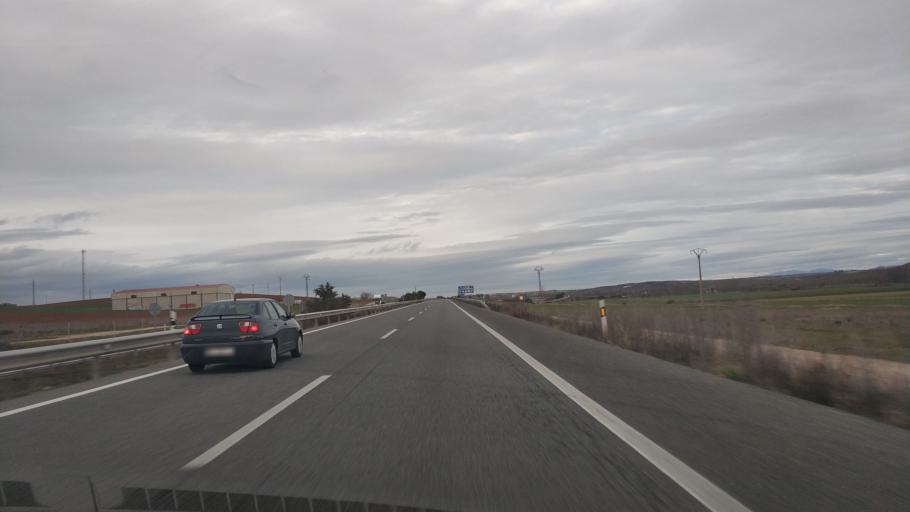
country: ES
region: Castille and Leon
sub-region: Provincia de Burgos
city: Estepar
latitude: 42.2706
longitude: -3.9117
